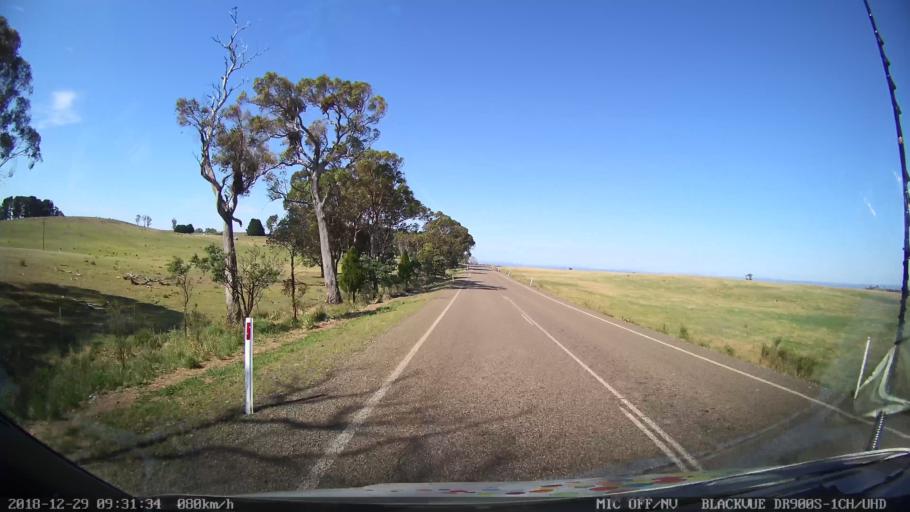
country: AU
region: New South Wales
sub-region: Upper Lachlan Shire
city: Crookwell
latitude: -34.6084
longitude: 149.3612
